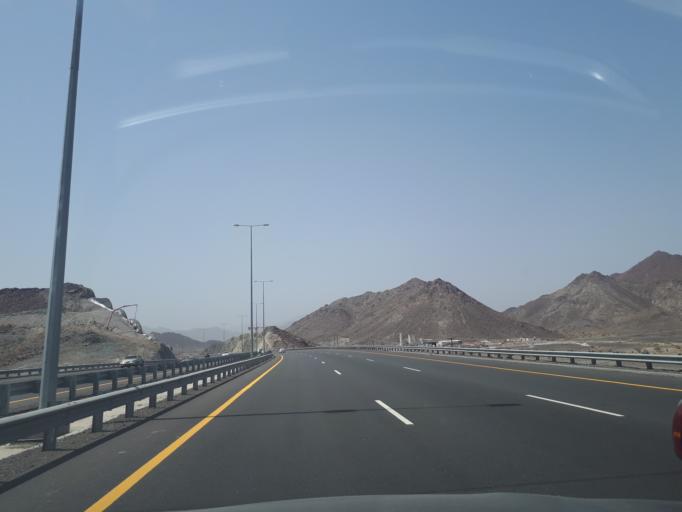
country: OM
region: Muhafazat ad Dakhiliyah
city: Bidbid
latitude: 23.3552
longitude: 58.0910
